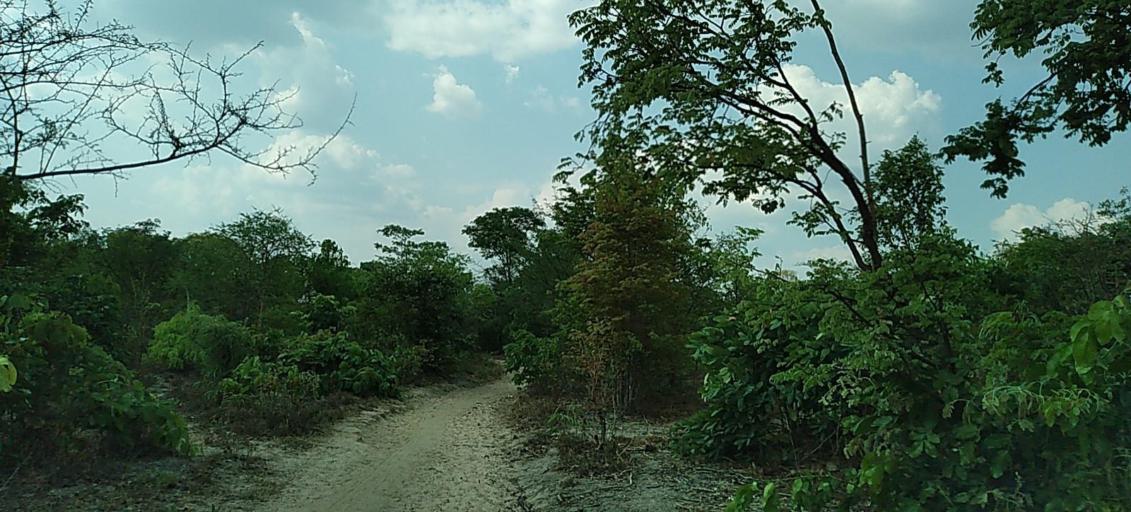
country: ZM
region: Copperbelt
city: Luanshya
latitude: -13.2177
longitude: 28.3312
